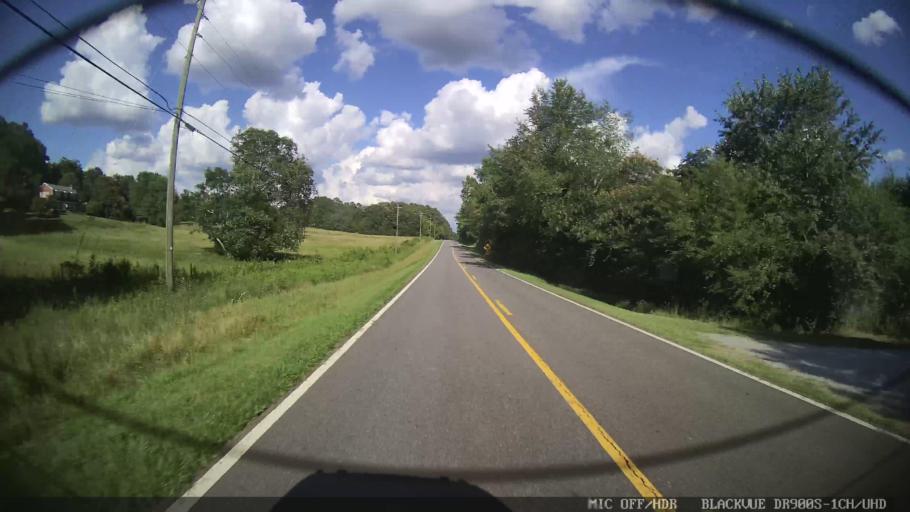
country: US
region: Georgia
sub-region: Bartow County
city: Euharlee
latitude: 34.1762
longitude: -84.9959
